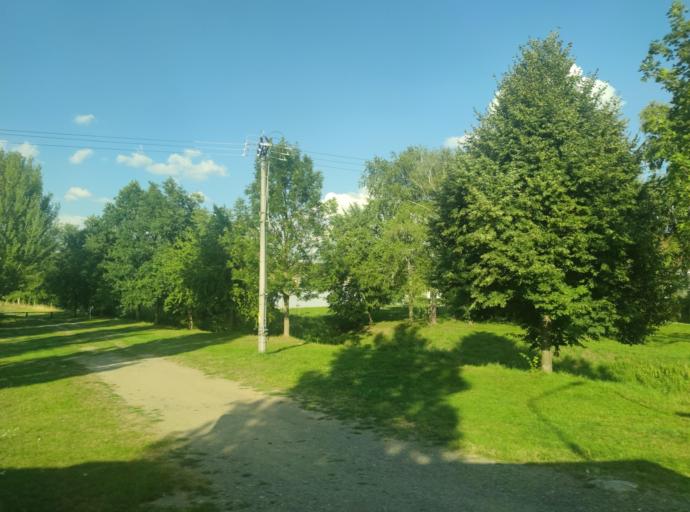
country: CZ
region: South Moravian
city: Vinicne Sumice
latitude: 49.1814
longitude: 16.8465
